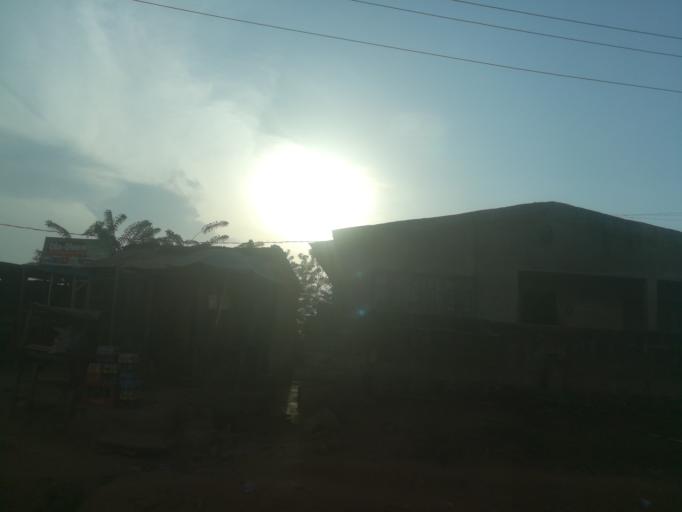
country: NG
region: Oyo
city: Moniya
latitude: 7.5390
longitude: 3.9001
